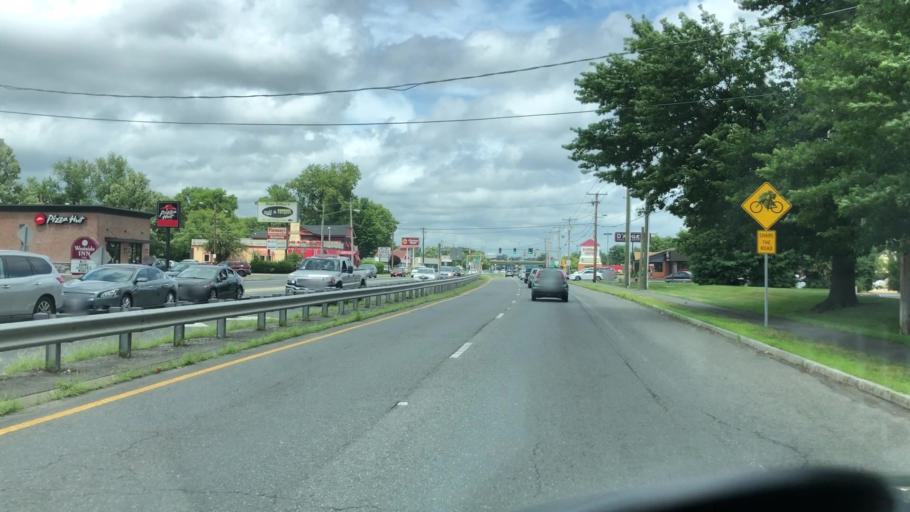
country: US
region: Massachusetts
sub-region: Hampden County
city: Chicopee
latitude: 42.1318
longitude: -72.6259
